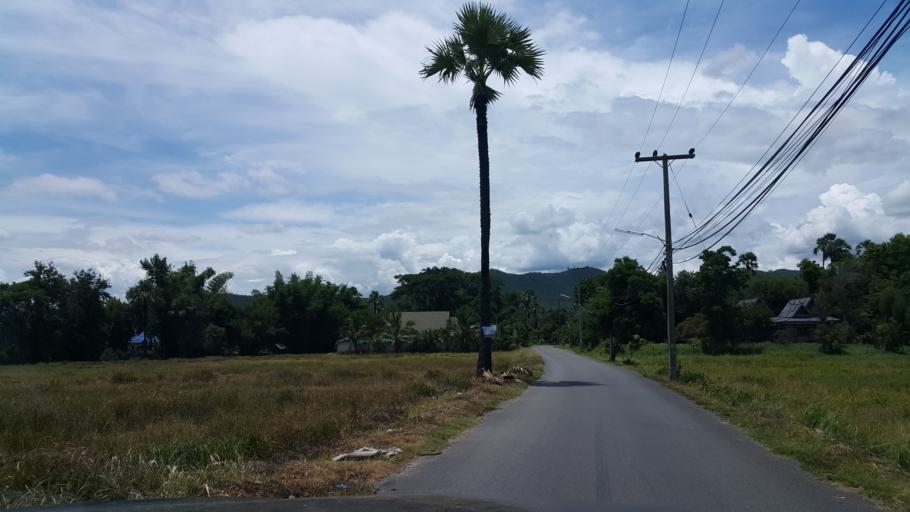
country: TH
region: Chiang Mai
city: Mae On
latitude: 18.7255
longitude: 99.2014
